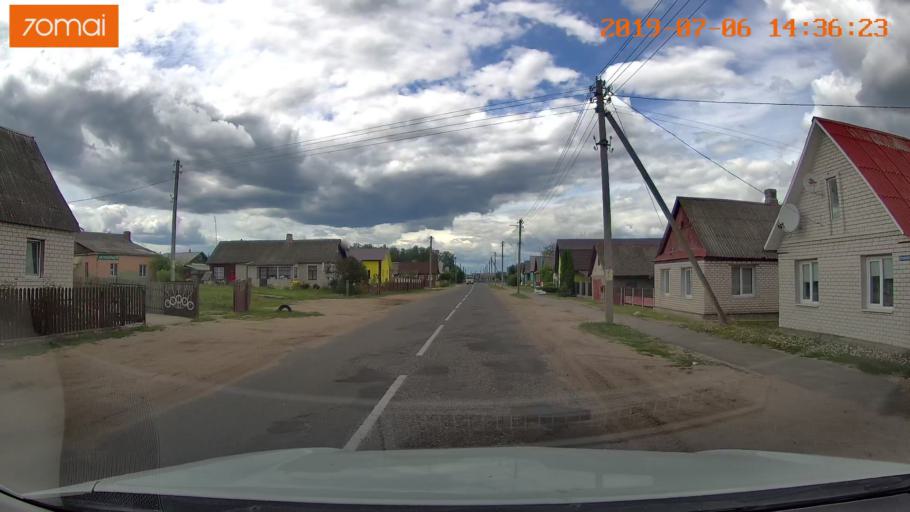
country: BY
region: Minsk
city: Ivyanyets
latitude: 53.8906
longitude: 26.7315
